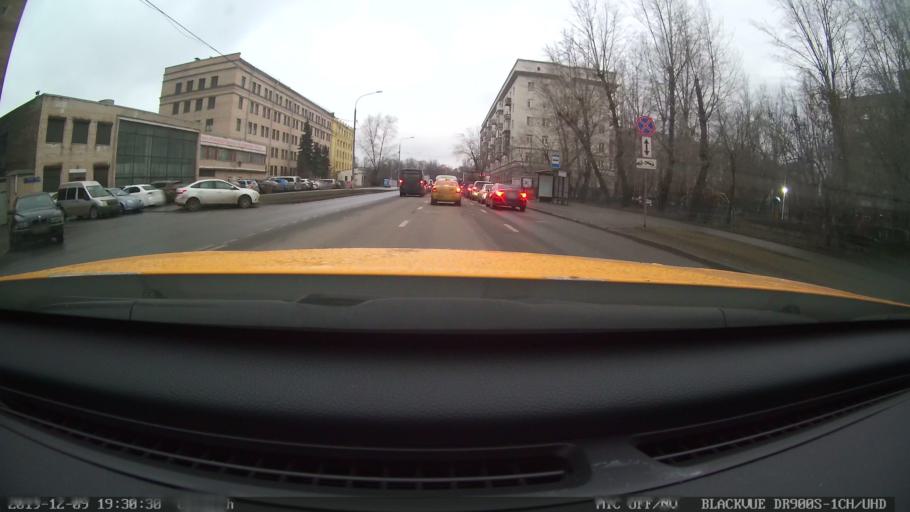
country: RU
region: Moscow
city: Ryazanskiy
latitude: 55.7572
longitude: 37.7578
